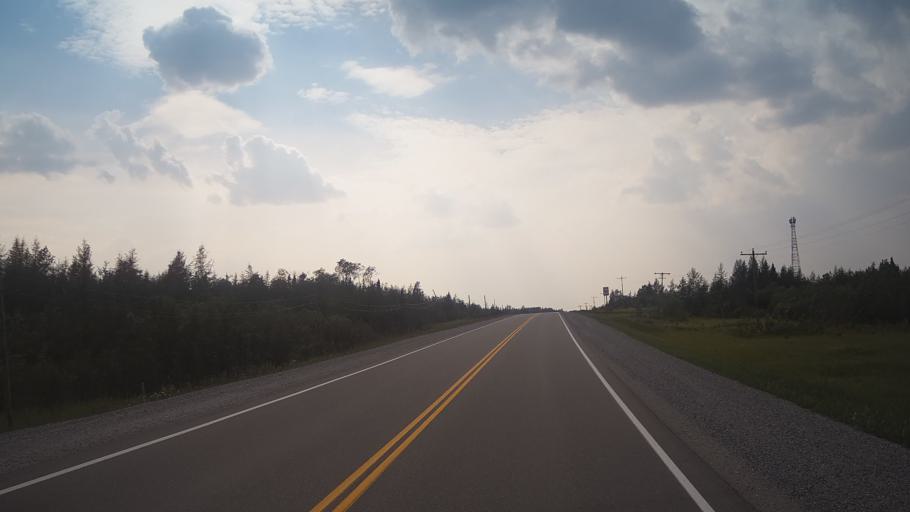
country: CA
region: Ontario
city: Kapuskasing
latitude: 49.5514
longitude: -82.9952
